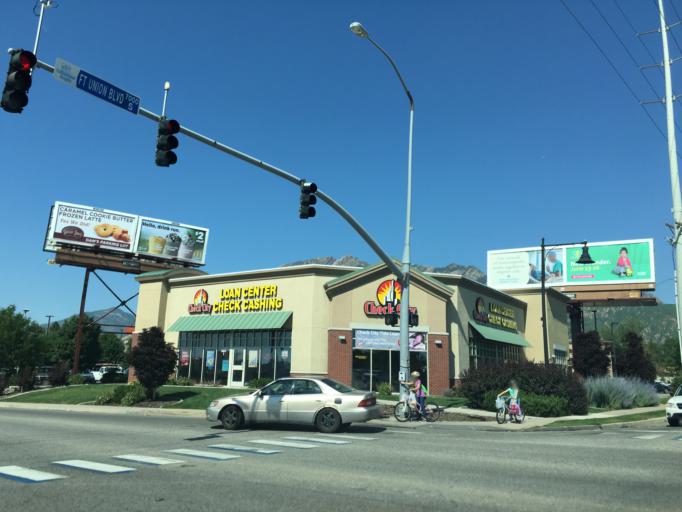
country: US
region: Utah
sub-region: Salt Lake County
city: Little Cottonwood Creek Valley
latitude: 40.6242
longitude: -111.8343
